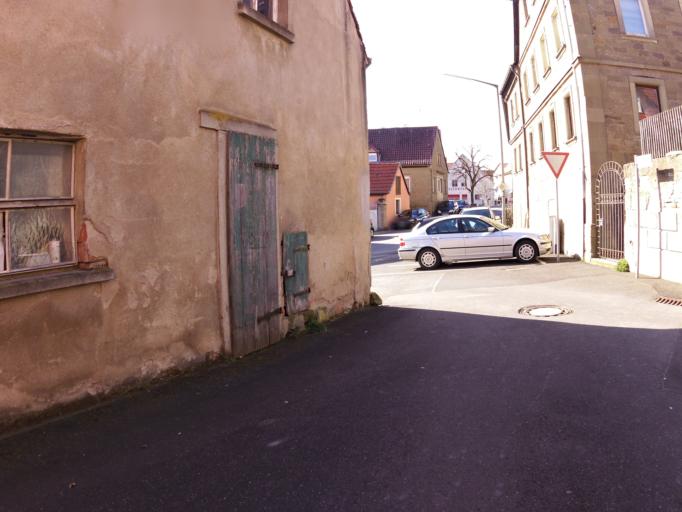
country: DE
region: Bavaria
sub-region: Regierungsbezirk Unterfranken
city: Buchbrunn
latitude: 49.7497
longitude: 10.1239
